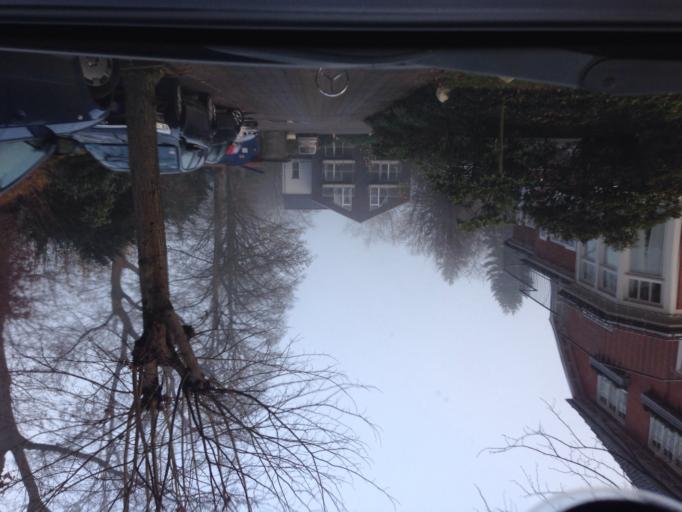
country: DE
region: Schleswig-Holstein
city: Ahrensburg
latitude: 53.6640
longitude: 10.2407
